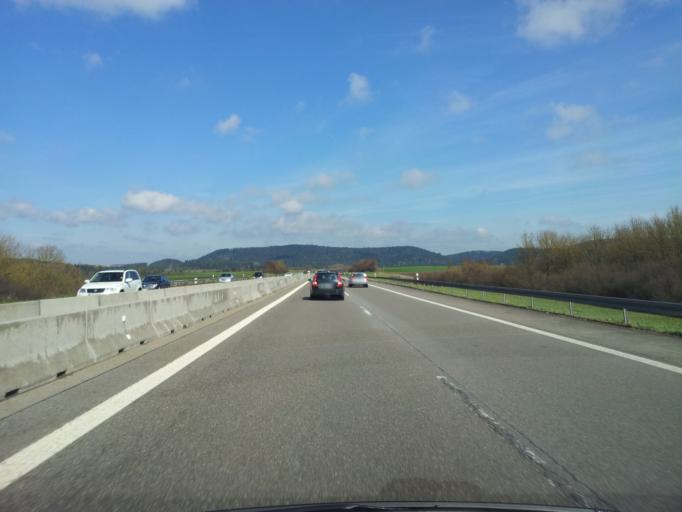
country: DE
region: Baden-Wuerttemberg
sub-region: Freiburg Region
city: Epfendorf
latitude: 48.2579
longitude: 8.6418
